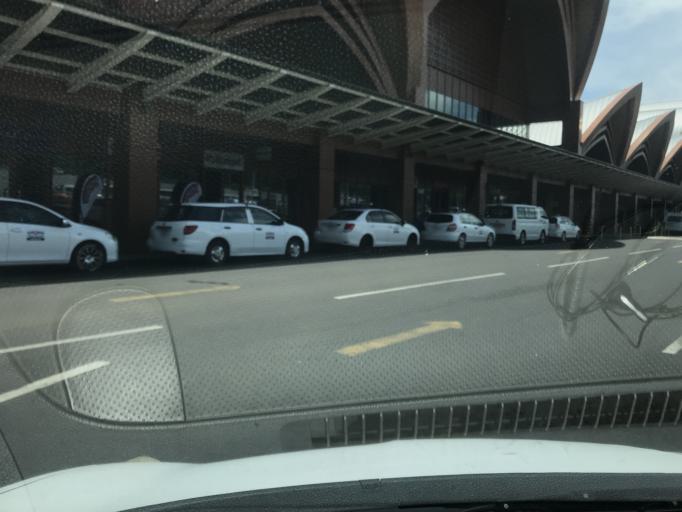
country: WS
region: A'ana
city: Satapuala
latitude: -13.8328
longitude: -171.9975
